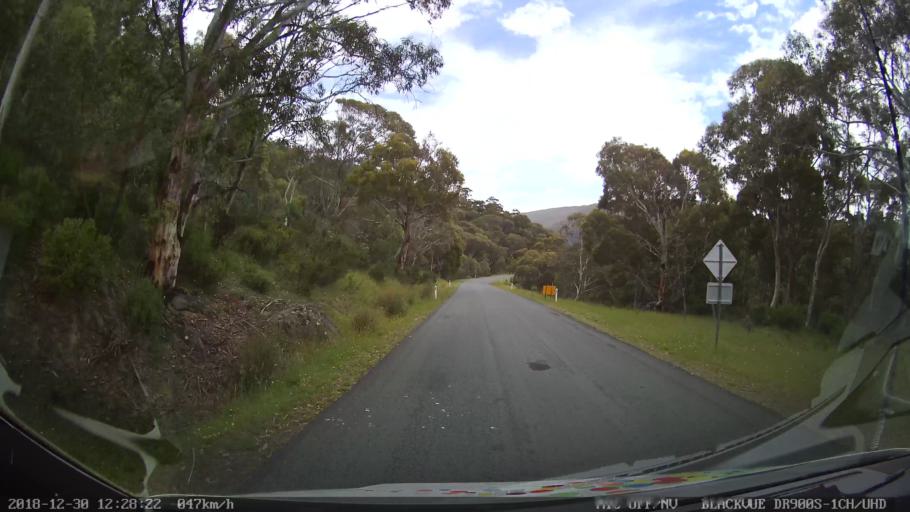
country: AU
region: New South Wales
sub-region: Snowy River
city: Jindabyne
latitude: -36.3262
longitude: 148.4855
